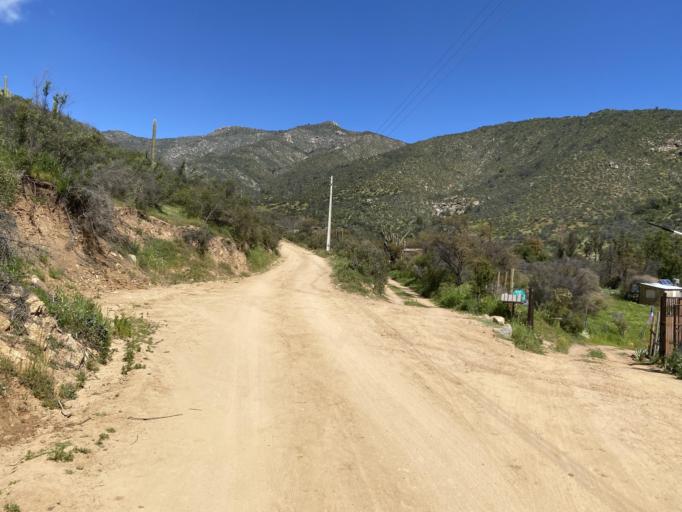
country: CL
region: Santiago Metropolitan
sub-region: Provincia de Chacabuco
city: Lampa
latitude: -33.1971
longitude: -71.0906
